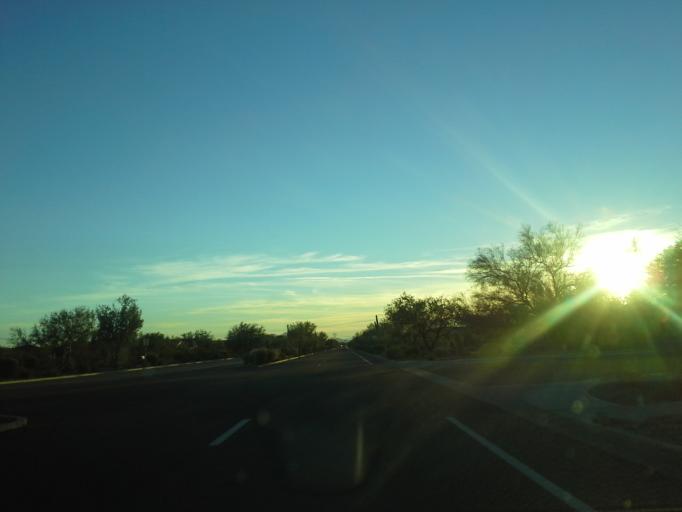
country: US
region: Arizona
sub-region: Pinal County
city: Apache Junction
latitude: 33.3709
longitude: -111.4718
